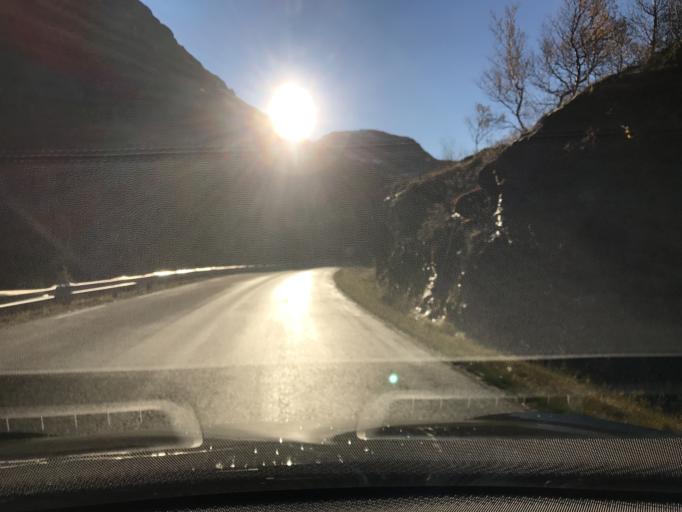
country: NO
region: Sogn og Fjordane
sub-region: Laerdal
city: Laerdalsoyri
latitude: 60.8132
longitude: 7.5540
